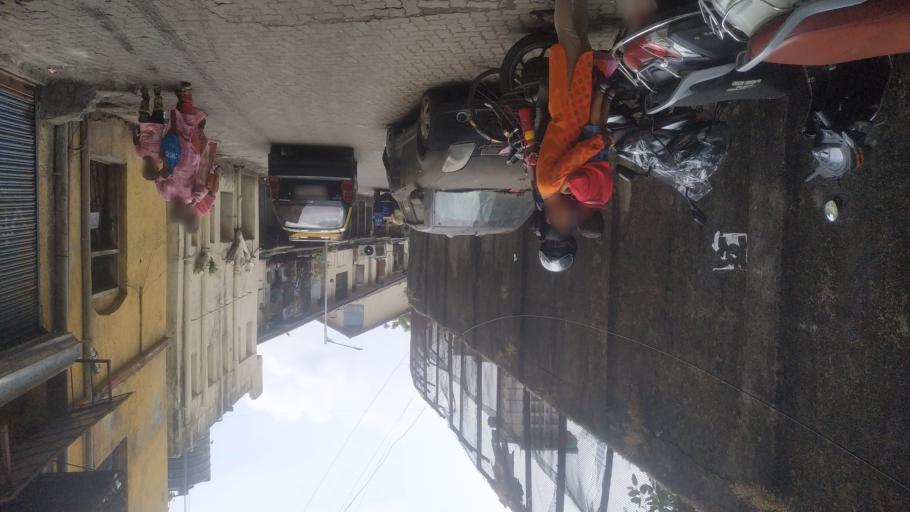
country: IN
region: Maharashtra
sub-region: Mumbai Suburban
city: Mumbai
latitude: 18.9887
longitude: 72.8363
